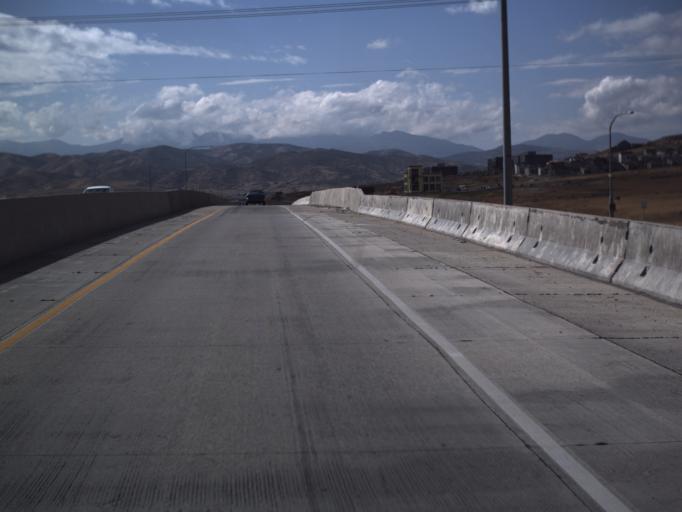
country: US
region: Utah
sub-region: Utah County
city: Lehi
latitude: 40.4323
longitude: -111.8487
